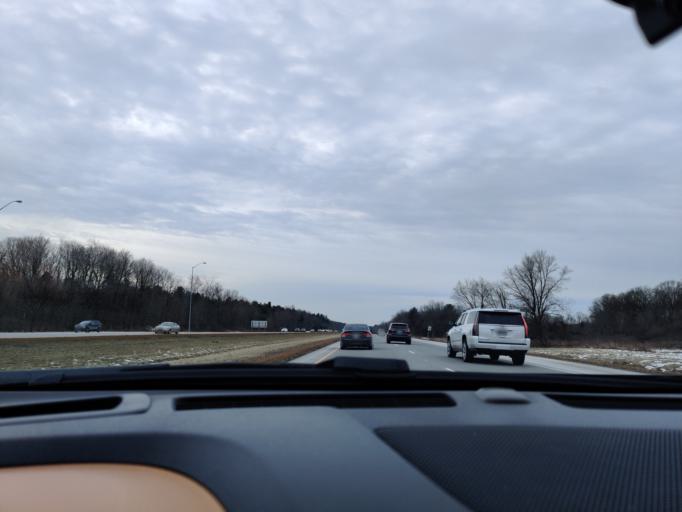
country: US
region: New York
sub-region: Jefferson County
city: Alexandria Bay
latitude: 44.4715
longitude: -75.8719
